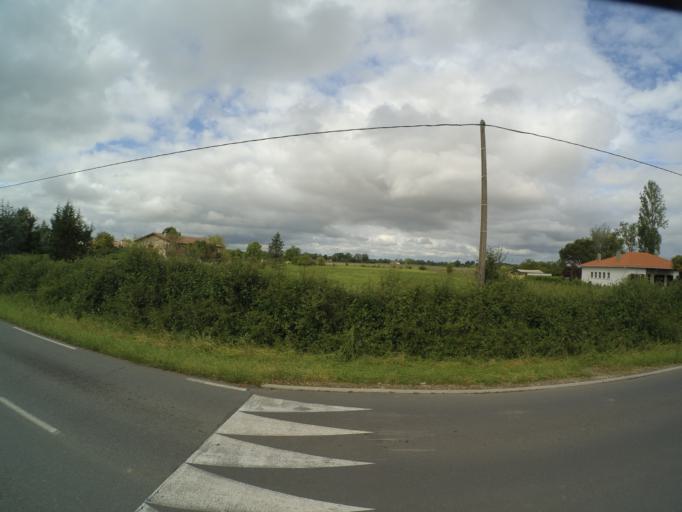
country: FR
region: Aquitaine
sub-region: Departement de la Gironde
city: Macau
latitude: 45.0066
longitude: -0.6092
